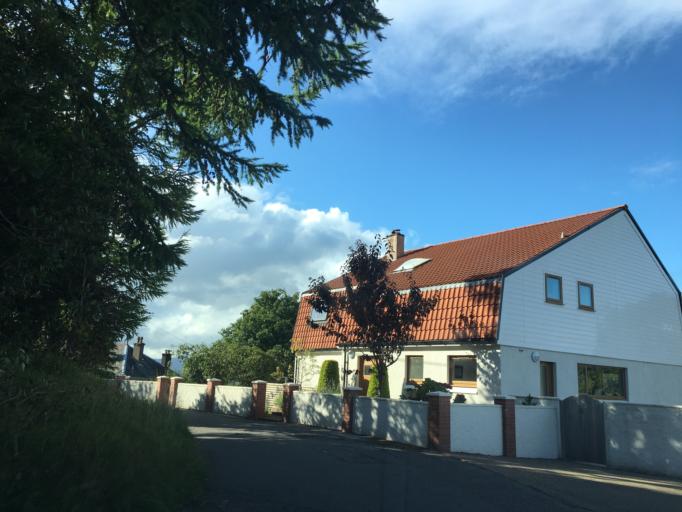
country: GB
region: Scotland
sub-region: Argyll and Bute
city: Oban
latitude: 56.4095
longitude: -5.4800
